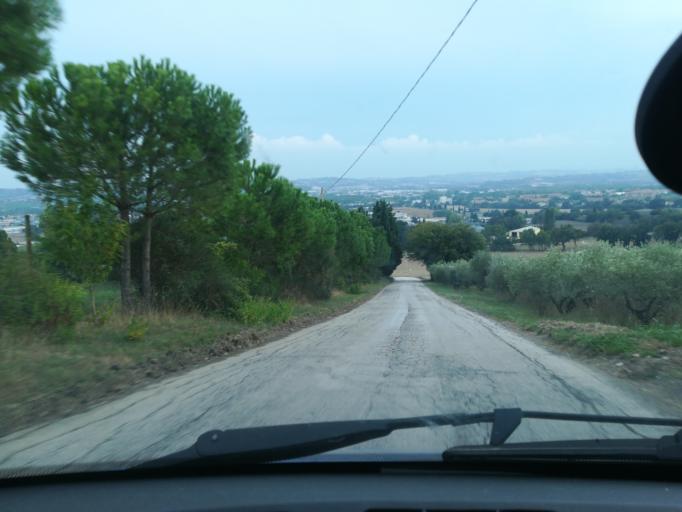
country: IT
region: The Marches
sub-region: Provincia di Macerata
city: Piediripa
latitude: 43.2893
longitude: 13.4883
